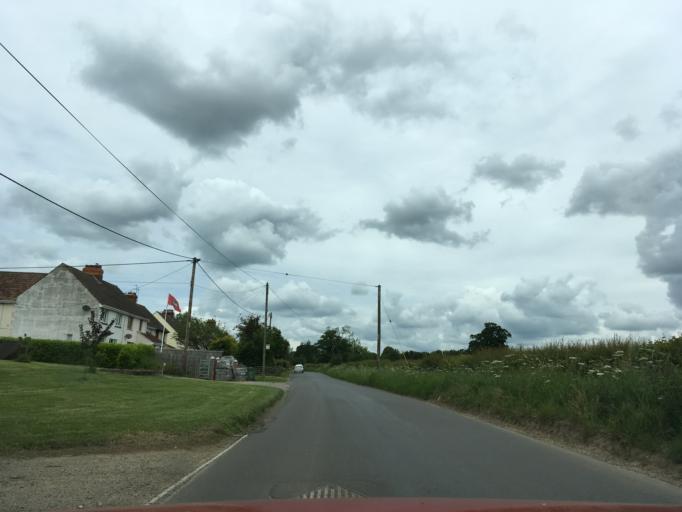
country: GB
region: England
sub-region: Wiltshire
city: Charlton
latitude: 51.5526
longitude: -2.0508
